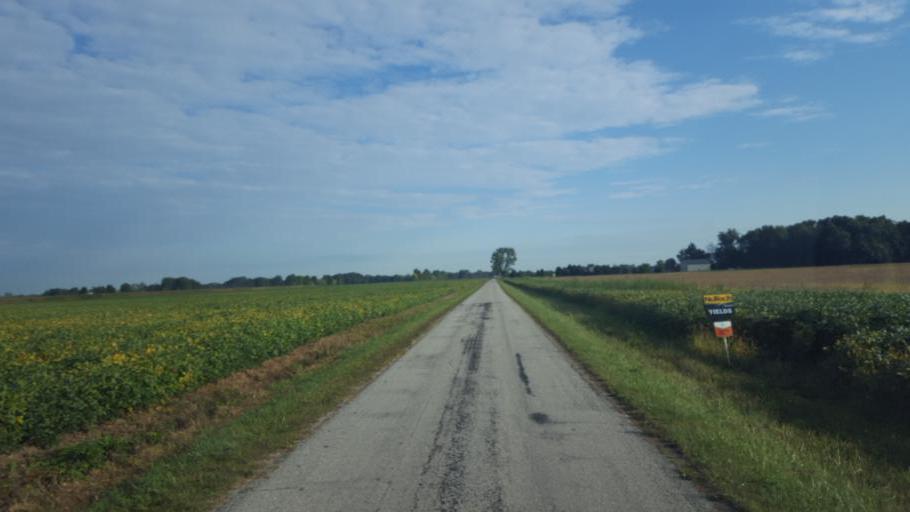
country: US
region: Ohio
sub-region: Morrow County
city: Mount Gilead
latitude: 40.6381
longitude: -82.8899
